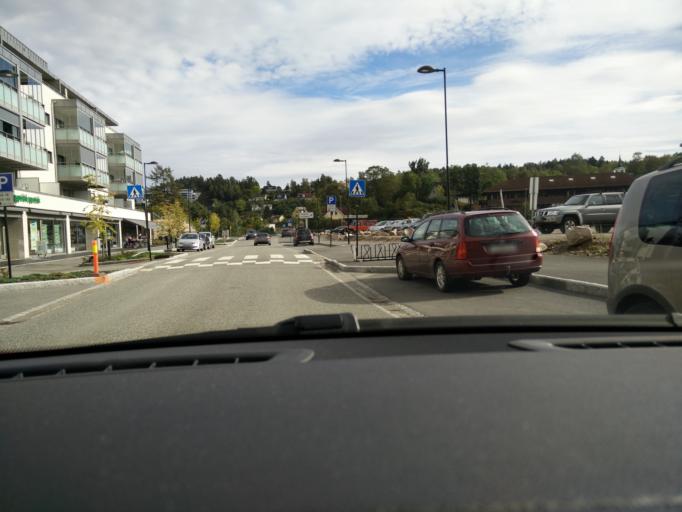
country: NO
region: Akershus
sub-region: Asker
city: Blakstad
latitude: 59.7879
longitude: 10.4346
